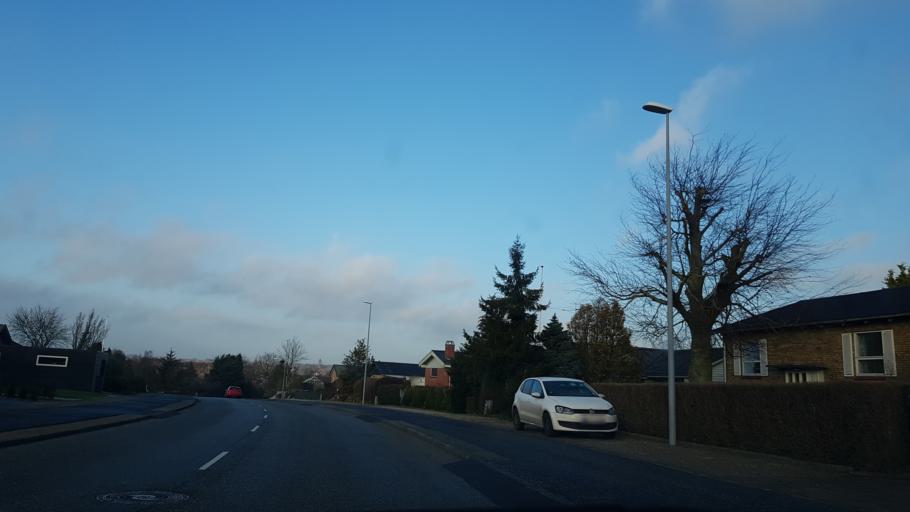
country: DK
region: South Denmark
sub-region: Haderslev Kommune
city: Haderslev
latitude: 55.2379
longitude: 9.4994
